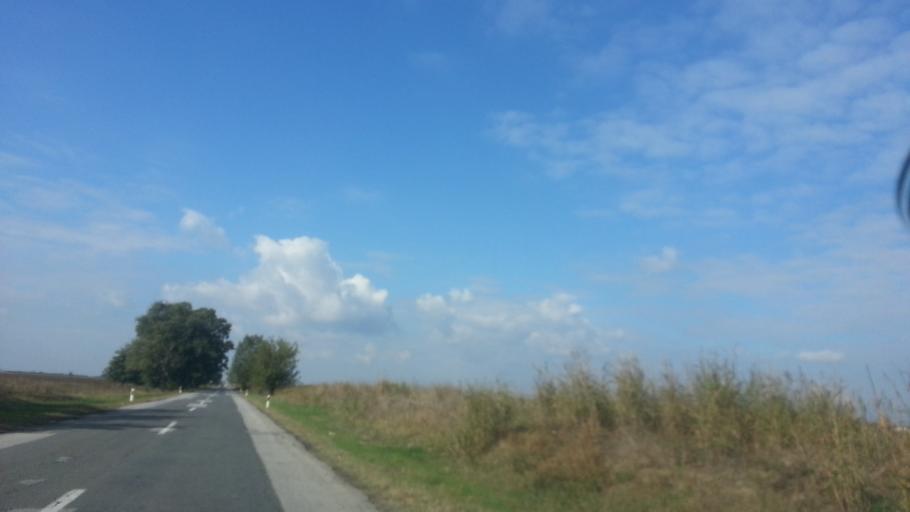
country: RS
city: Stari Banovci
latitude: 44.9864
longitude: 20.2415
